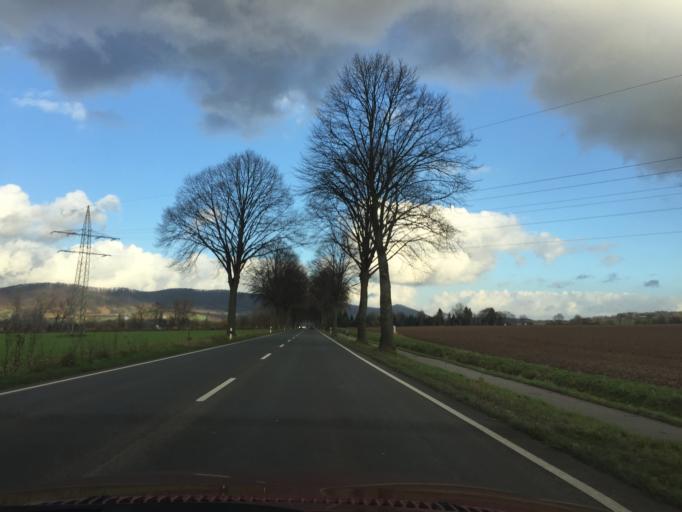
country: DE
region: Lower Saxony
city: Bevern
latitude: 51.8461
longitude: 9.4818
